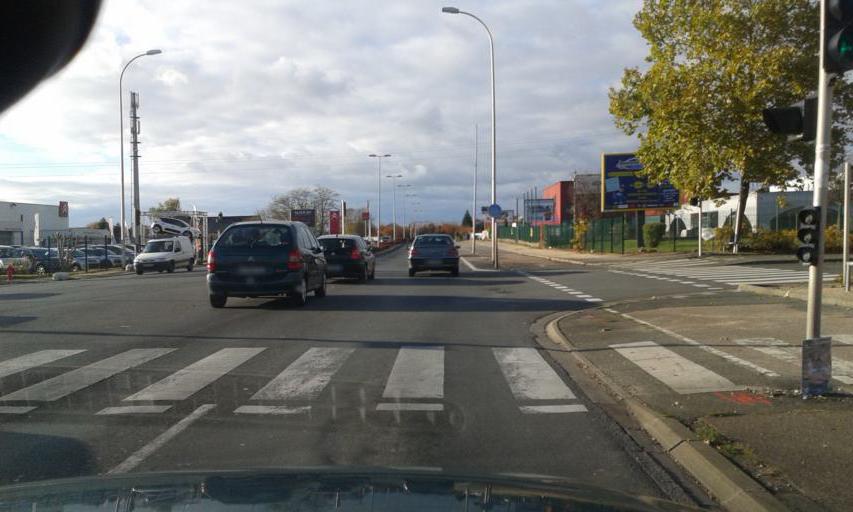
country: FR
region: Centre
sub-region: Departement du Loiret
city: Olivet
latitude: 47.8443
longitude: 1.9206
